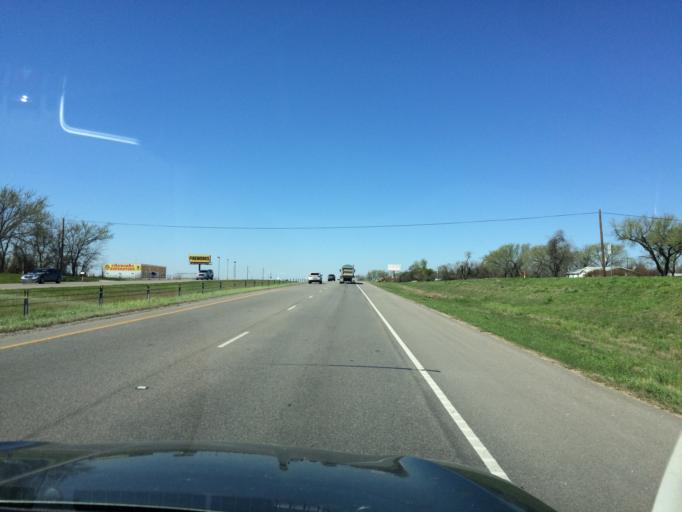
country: US
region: Texas
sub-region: Travis County
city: Garfield
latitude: 30.1867
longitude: -97.5551
